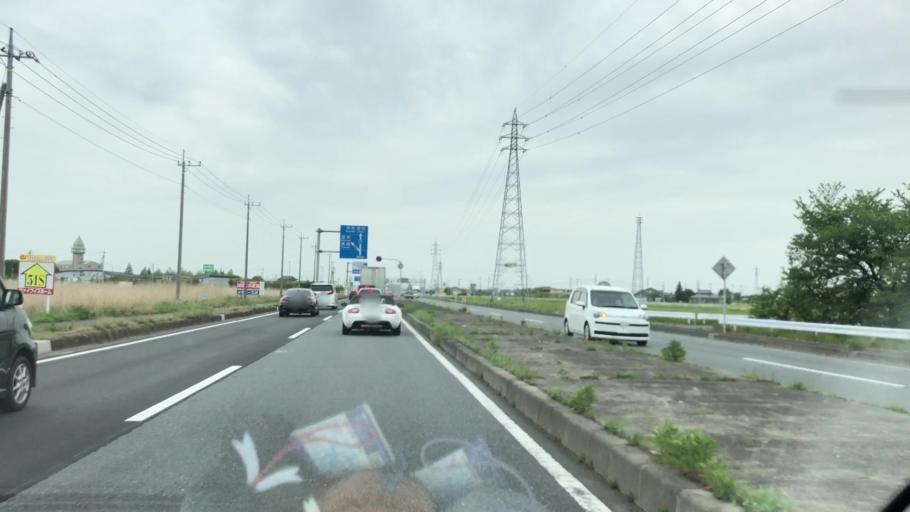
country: JP
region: Gunma
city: Sakai-nakajima
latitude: 36.2660
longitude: 139.2931
